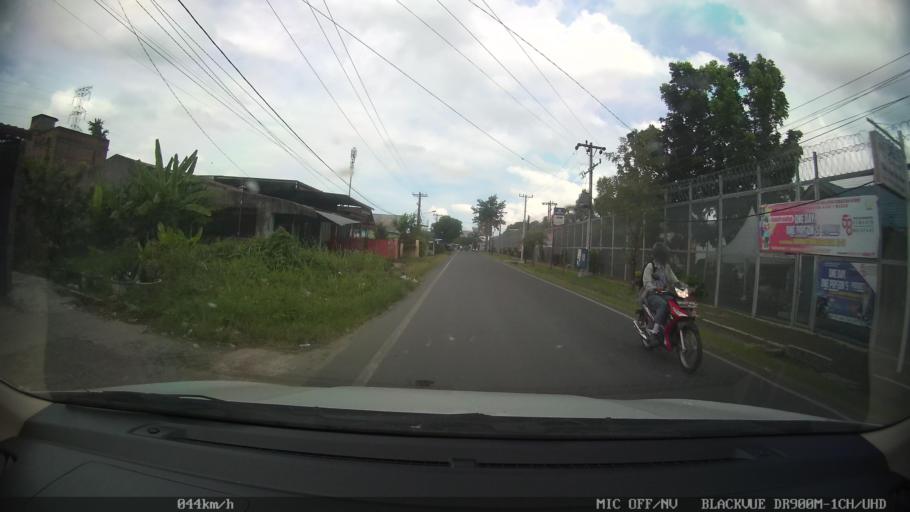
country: ID
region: North Sumatra
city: Sunggal
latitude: 3.6184
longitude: 98.6107
